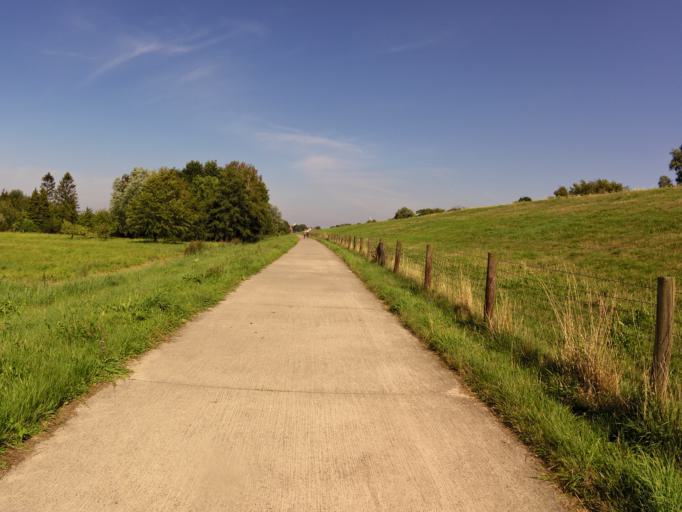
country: DE
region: Lower Saxony
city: Brake (Unterweser)
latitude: 53.2956
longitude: 8.4856
